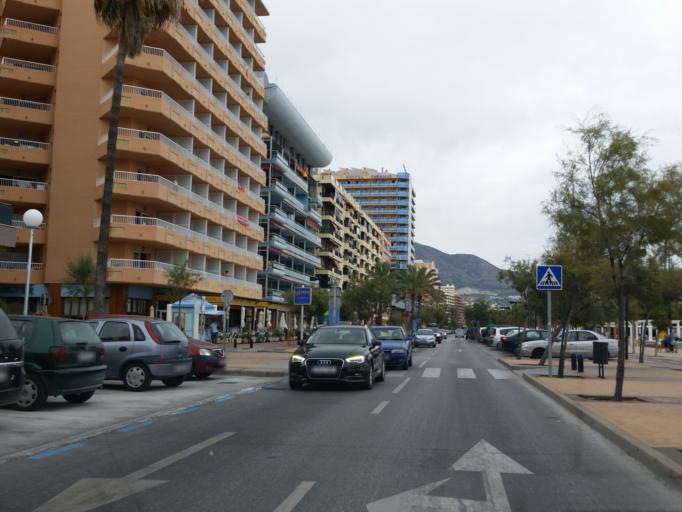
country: ES
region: Andalusia
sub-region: Provincia de Malaga
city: Fuengirola
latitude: 36.5490
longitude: -4.6155
